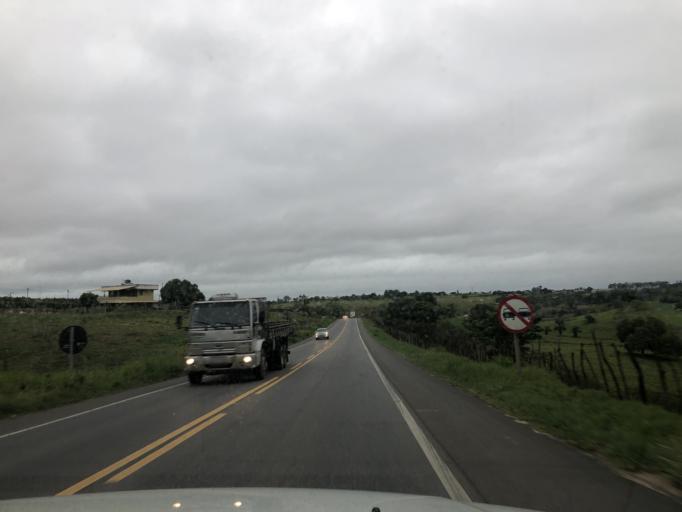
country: BR
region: Bahia
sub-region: Cruz Das Almas
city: Cruz das Almas
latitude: -12.6396
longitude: -39.0981
